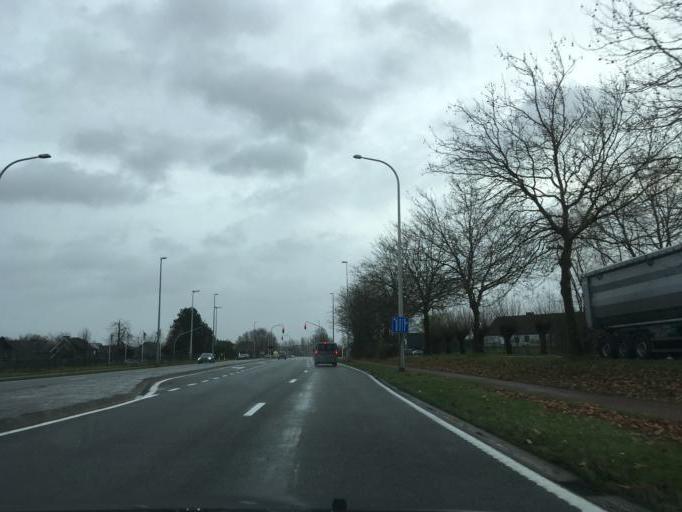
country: BE
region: Flanders
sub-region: Provincie West-Vlaanderen
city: Roeselare
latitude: 50.9232
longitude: 3.1374
